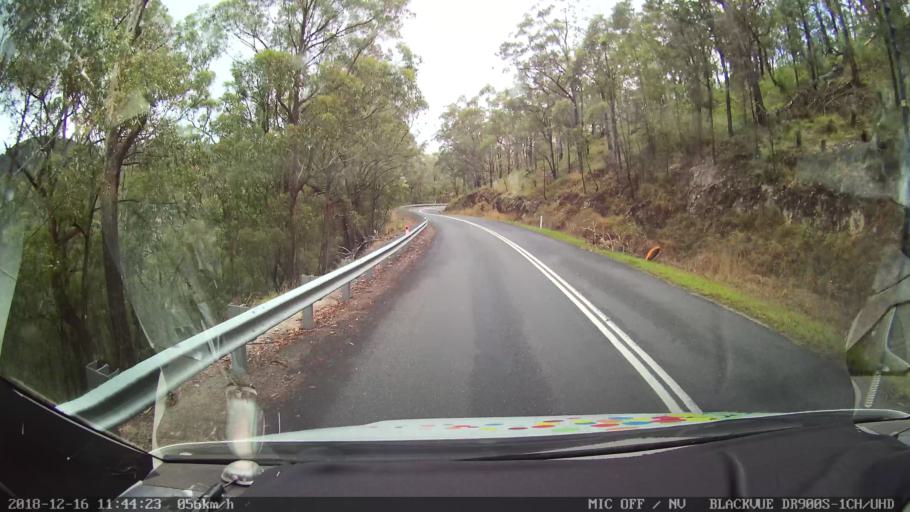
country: AU
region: New South Wales
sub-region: Tenterfield Municipality
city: Carrolls Creek
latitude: -28.9387
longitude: 152.2197
